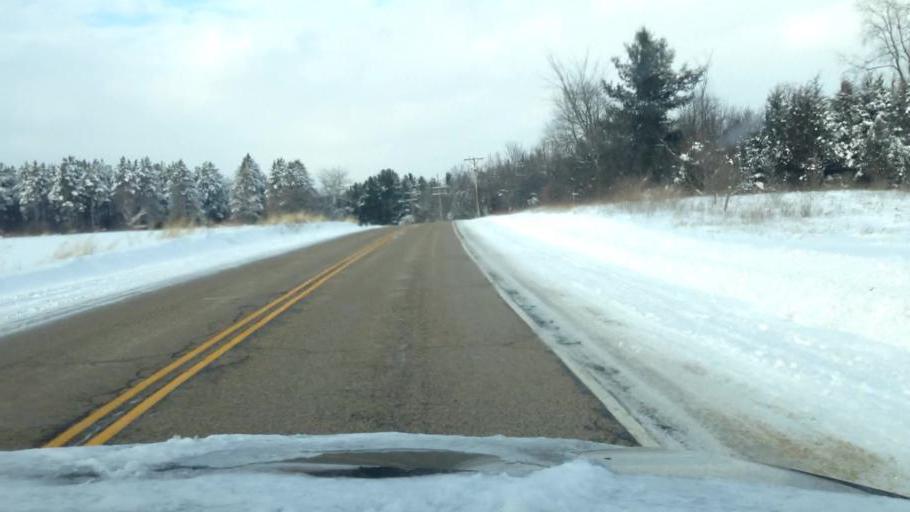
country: US
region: Wisconsin
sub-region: Walworth County
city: East Troy
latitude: 42.8306
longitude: -88.4240
